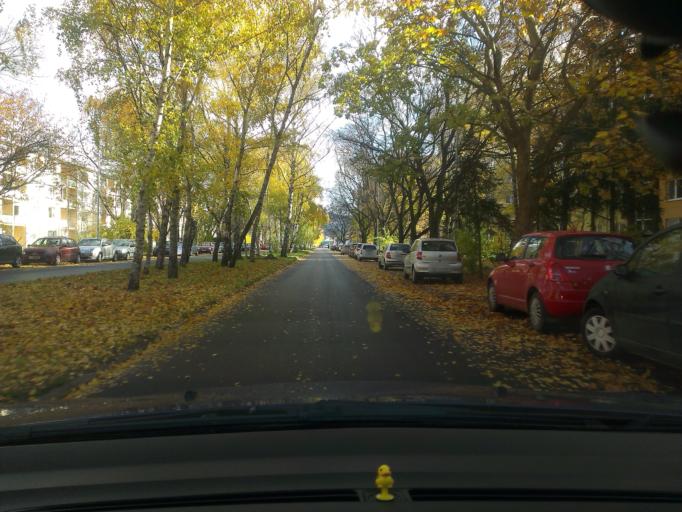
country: SK
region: Trnavsky
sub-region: Okres Trnava
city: Piestany
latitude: 48.5960
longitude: 17.8208
